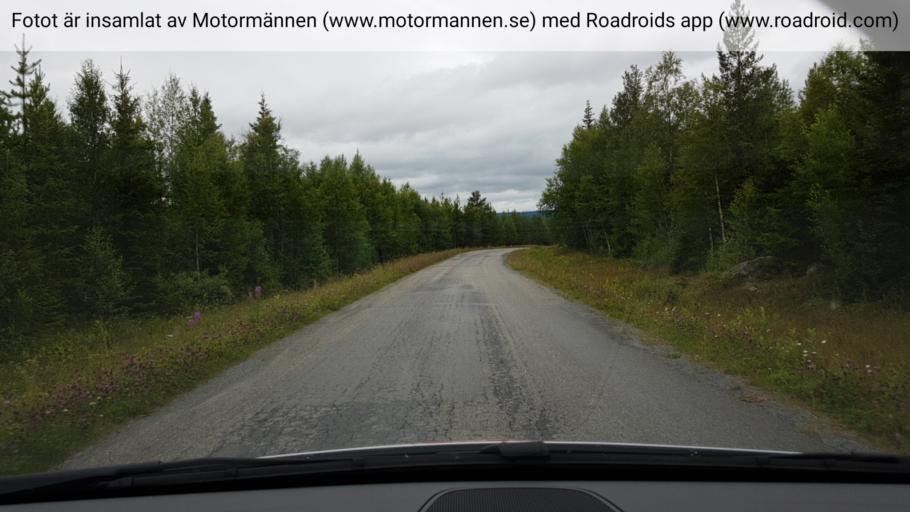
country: SE
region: Jaemtland
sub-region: Krokoms Kommun
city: Krokom
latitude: 63.7591
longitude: 14.3677
